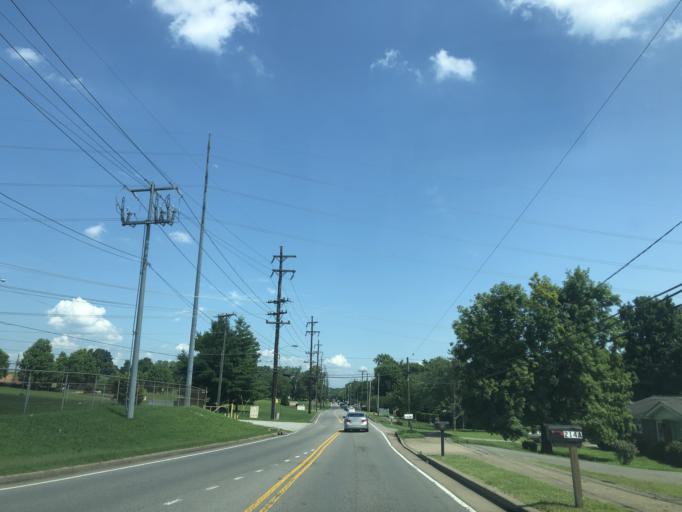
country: US
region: Tennessee
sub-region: Davidson County
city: Lakewood
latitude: 36.1641
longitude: -86.6503
